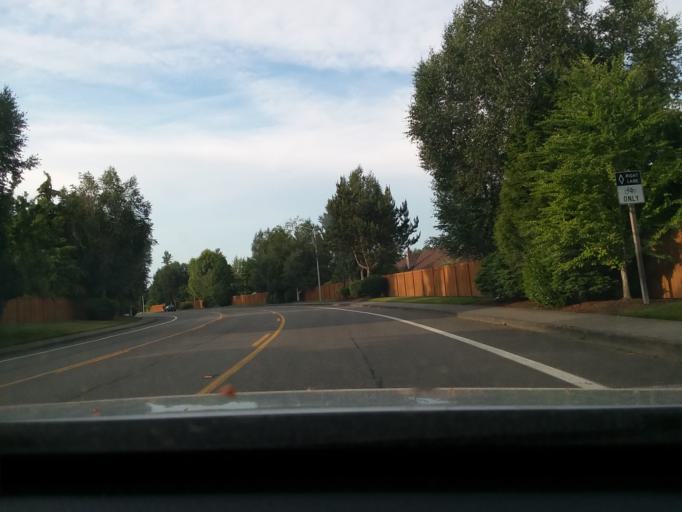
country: US
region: Washington
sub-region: Snohomish County
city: Silver Firs
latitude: 47.8589
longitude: -122.1385
